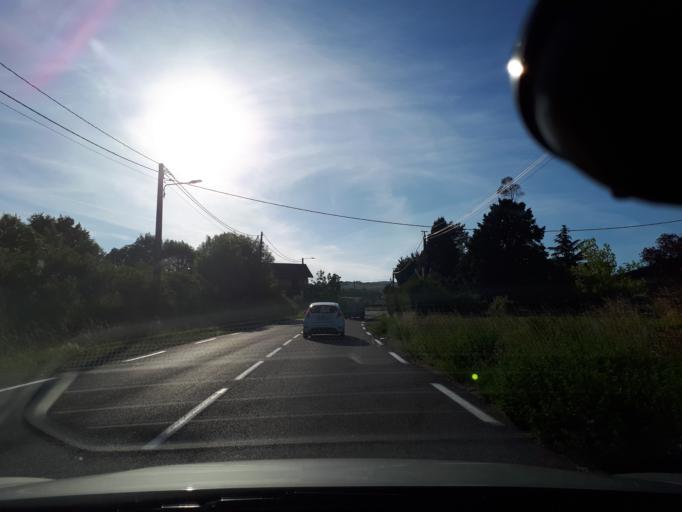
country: FR
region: Rhone-Alpes
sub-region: Departement de la Loire
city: Saint-Joseph
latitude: 45.5475
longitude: 4.6104
